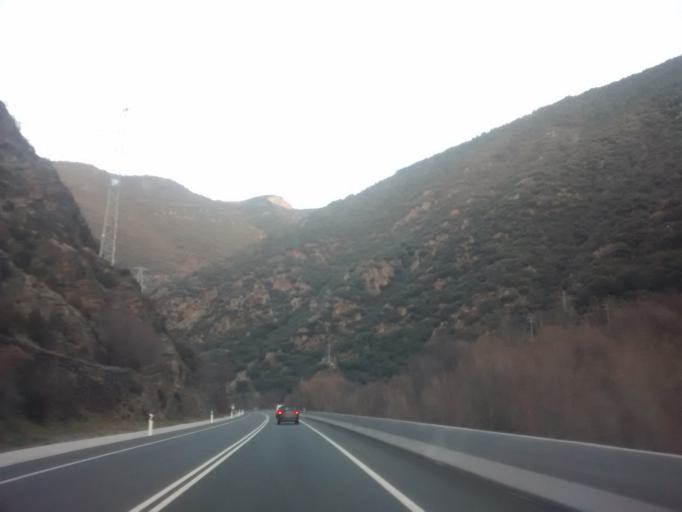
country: ES
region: Catalonia
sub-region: Provincia de Lleida
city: la Seu d'Urgell
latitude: 42.4040
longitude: 1.4649
